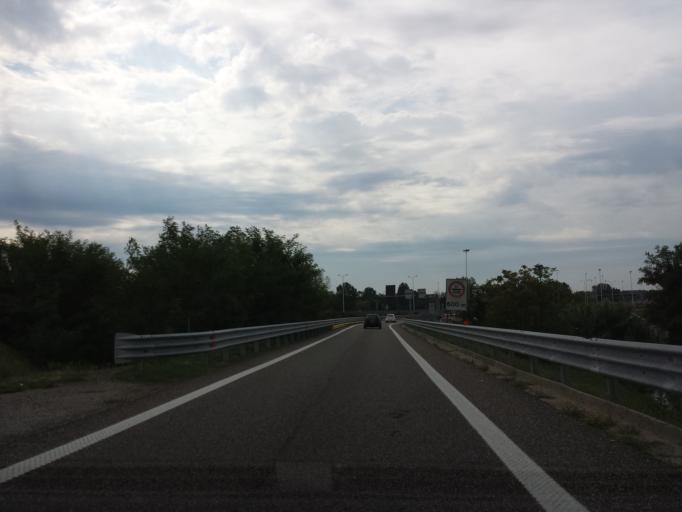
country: IT
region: Lombardy
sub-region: Citta metropolitana di Milano
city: Assago
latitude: 45.3947
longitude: 9.1394
